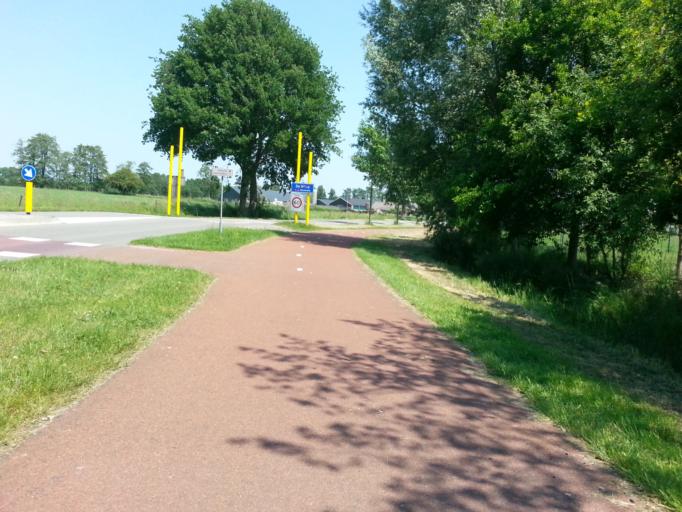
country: NL
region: Gelderland
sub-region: Gemeente Barneveld
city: Terschuur
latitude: 52.1181
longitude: 5.5134
